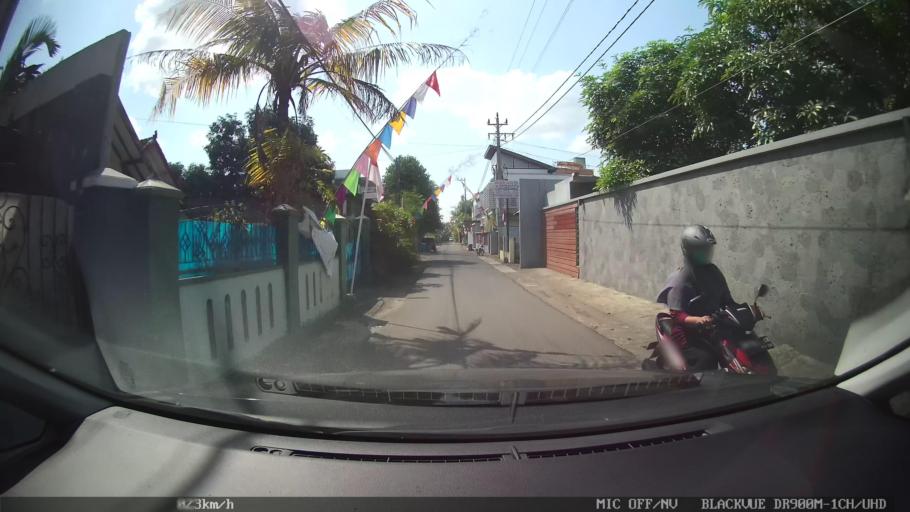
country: ID
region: Daerah Istimewa Yogyakarta
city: Kasihan
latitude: -7.8350
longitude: 110.3669
